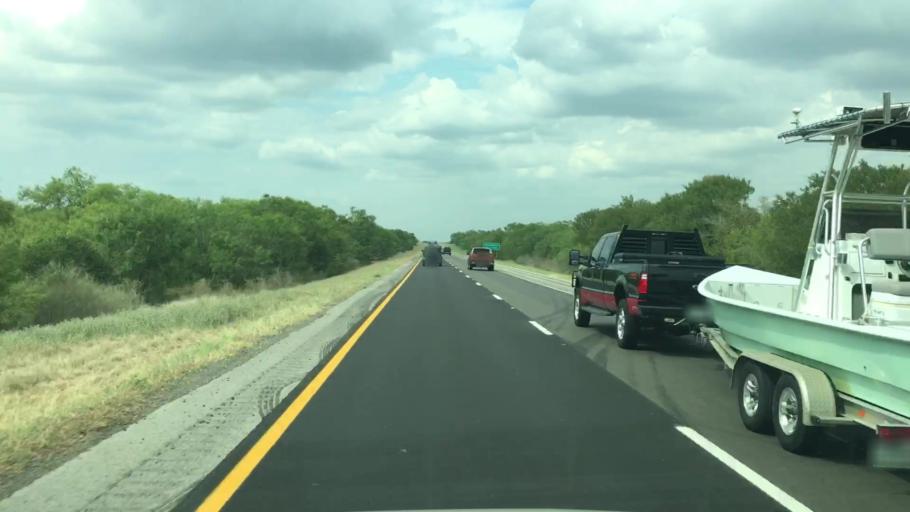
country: US
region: Texas
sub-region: Atascosa County
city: Pleasanton
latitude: 28.9311
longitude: -98.4352
